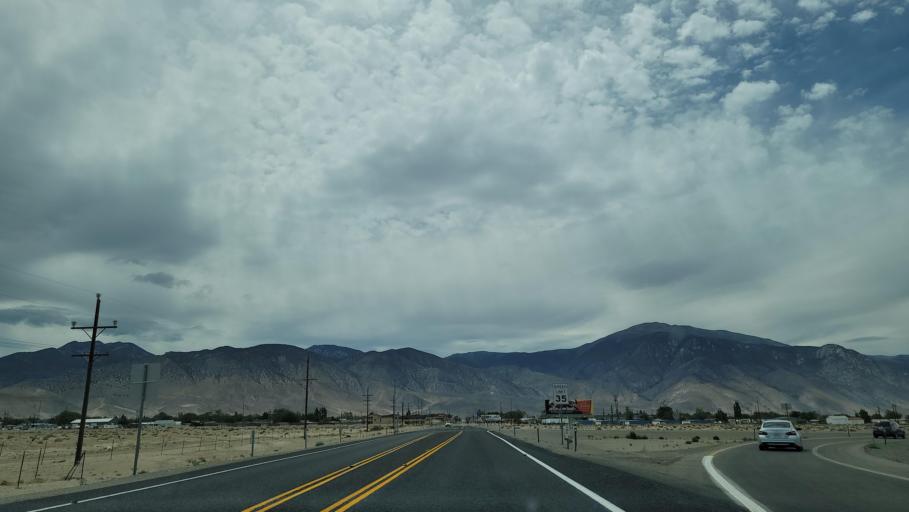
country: US
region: Nevada
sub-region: Mineral County
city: Hawthorne
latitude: 38.5246
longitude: -118.6095
